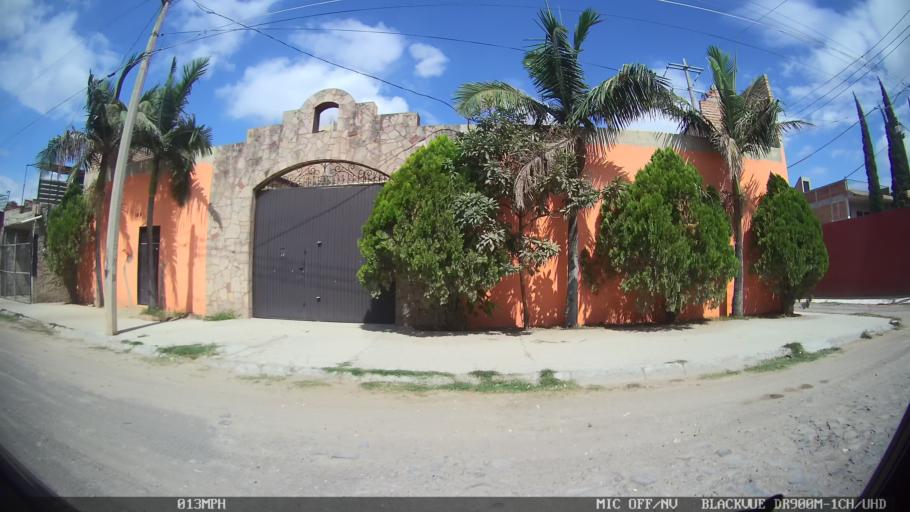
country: MX
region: Jalisco
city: Tonala
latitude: 20.6646
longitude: -103.2436
